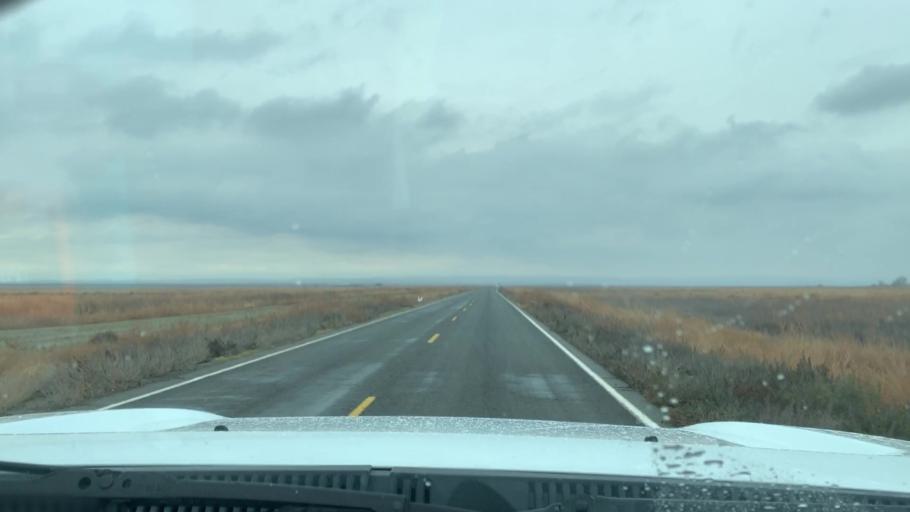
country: US
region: California
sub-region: Kings County
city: Kettleman City
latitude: 35.9340
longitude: -119.8053
